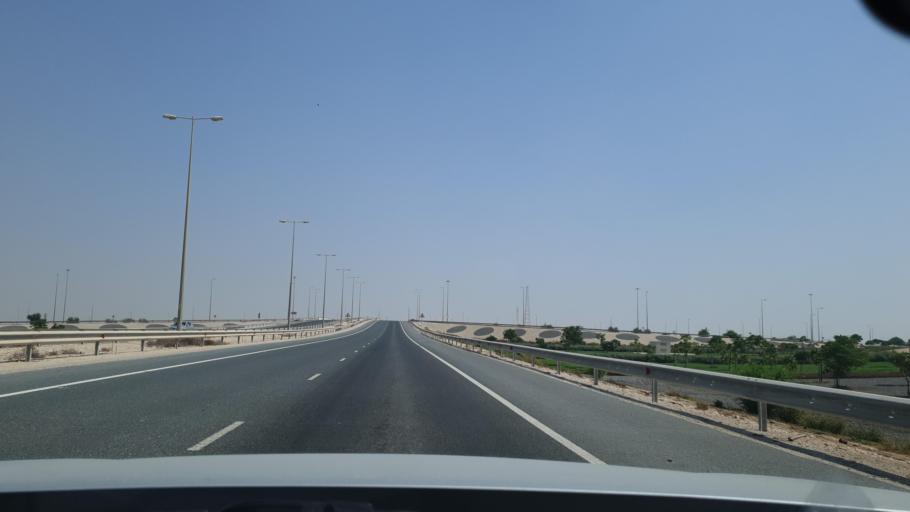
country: QA
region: Baladiyat az Za`ayin
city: Az Za`ayin
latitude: 25.6207
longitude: 51.3978
